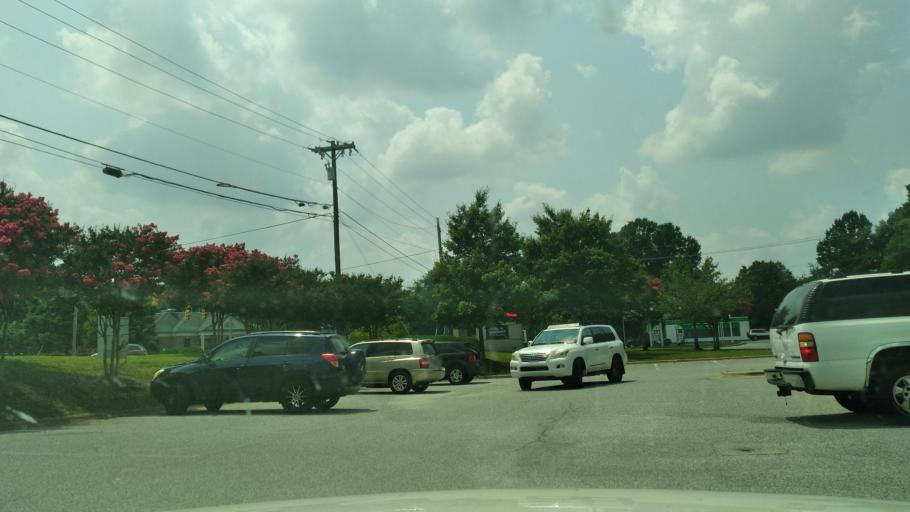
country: US
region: North Carolina
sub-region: Guilford County
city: Summerfield
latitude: 36.1263
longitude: -79.9058
